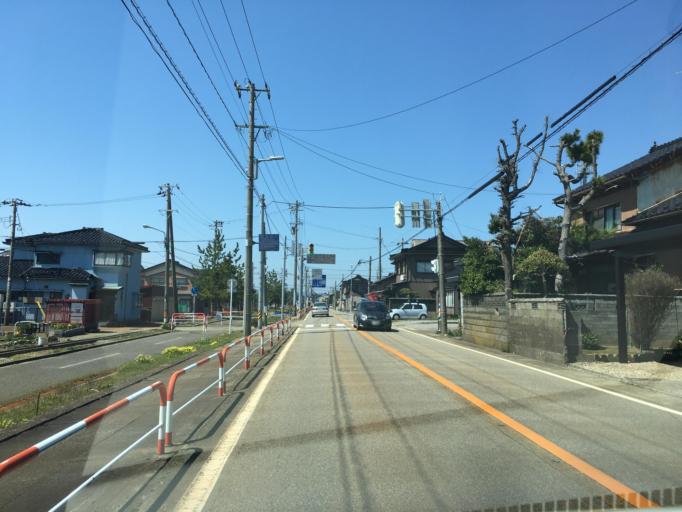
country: JP
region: Toyama
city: Kuragaki-kosugi
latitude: 36.7686
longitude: 137.1364
